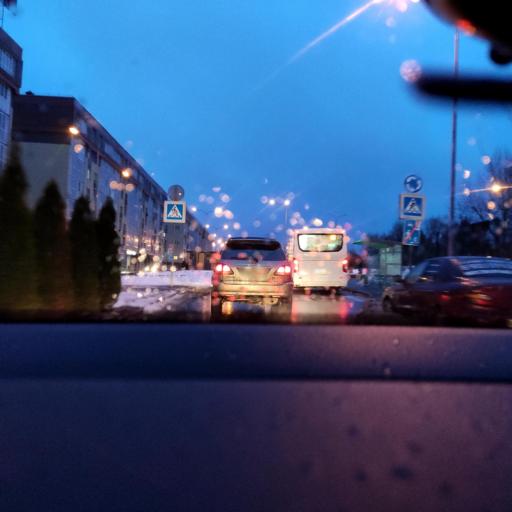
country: RU
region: Moskovskaya
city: Nakhabino
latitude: 55.8508
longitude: 37.1906
